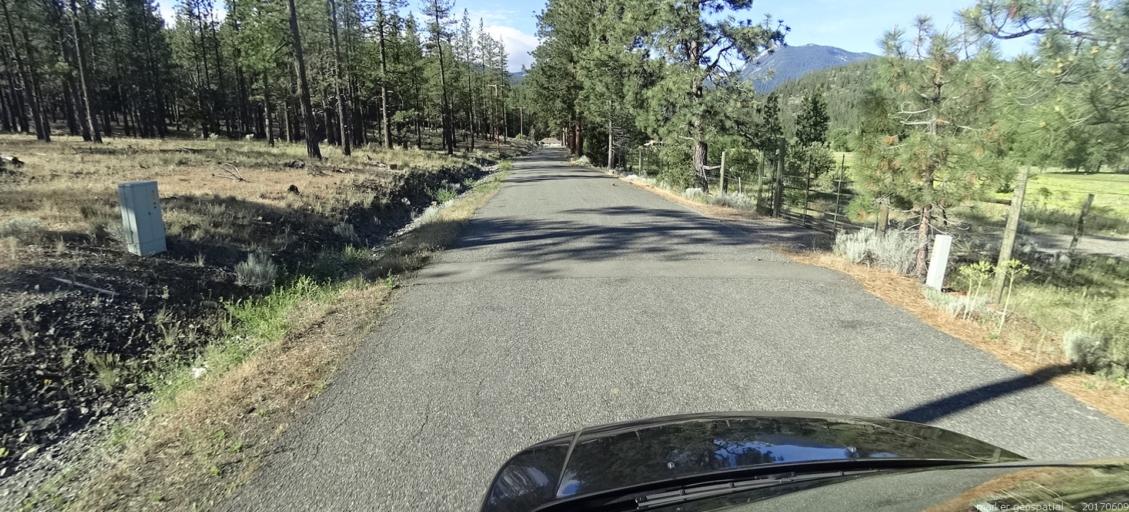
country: US
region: California
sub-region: Siskiyou County
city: Weed
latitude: 41.3292
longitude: -122.7183
